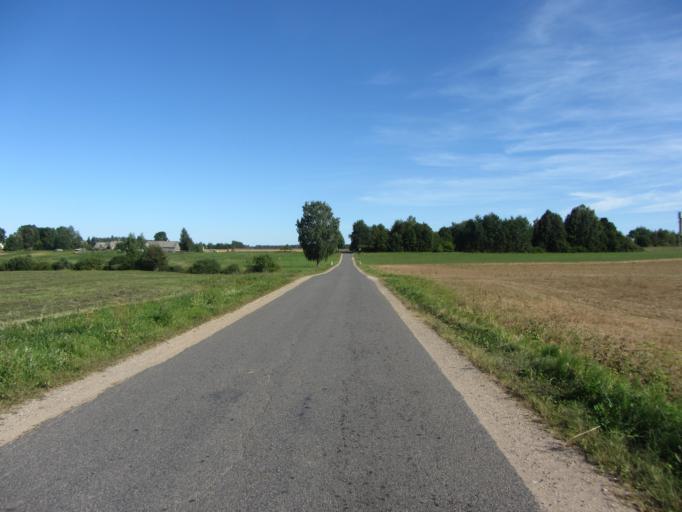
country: LT
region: Panevezys
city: Rokiskis
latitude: 55.7374
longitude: 25.3994
